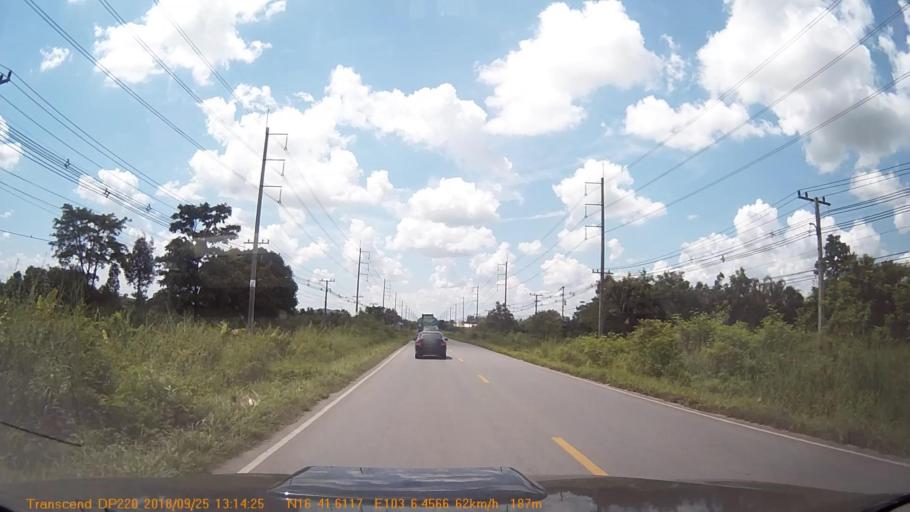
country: TH
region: Khon Kaen
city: Kranuan
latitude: 16.6935
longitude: 103.1077
